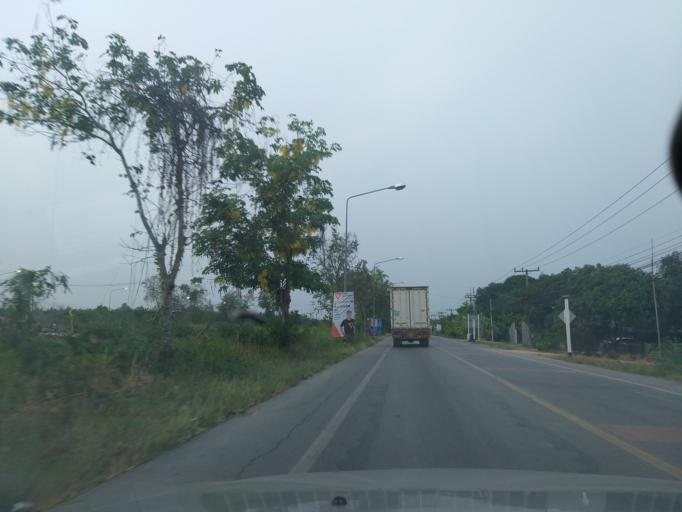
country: TH
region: Pathum Thani
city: Ban Lam Luk Ka
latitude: 14.0187
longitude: 100.8943
